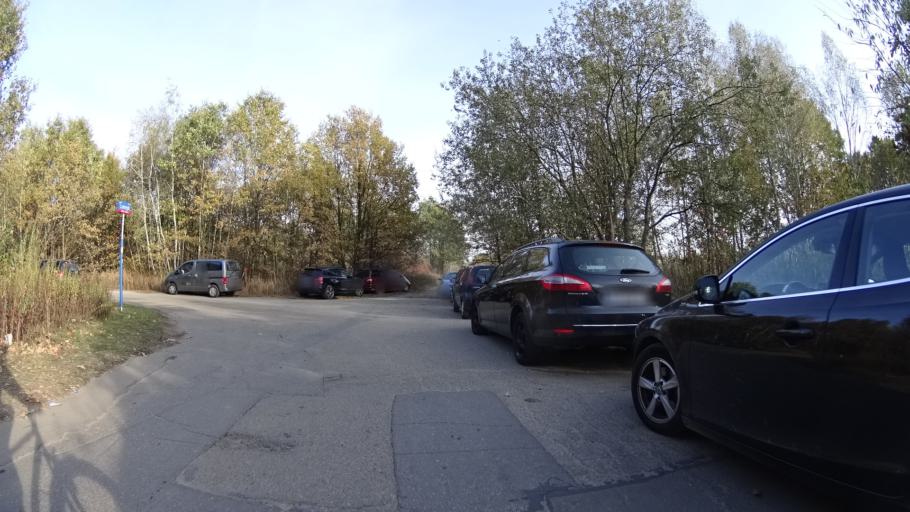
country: PL
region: Masovian Voivodeship
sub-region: Powiat warszawski zachodni
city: Lomianki
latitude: 52.2945
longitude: 20.8884
